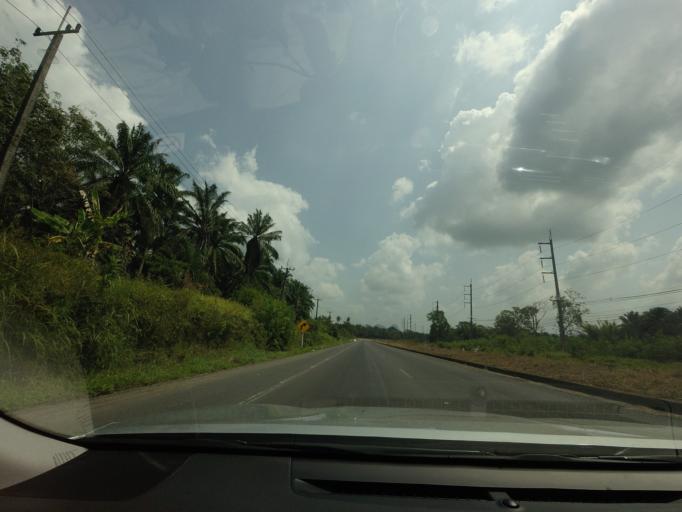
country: TH
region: Phangnga
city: Thap Put
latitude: 8.5068
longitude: 98.6872
